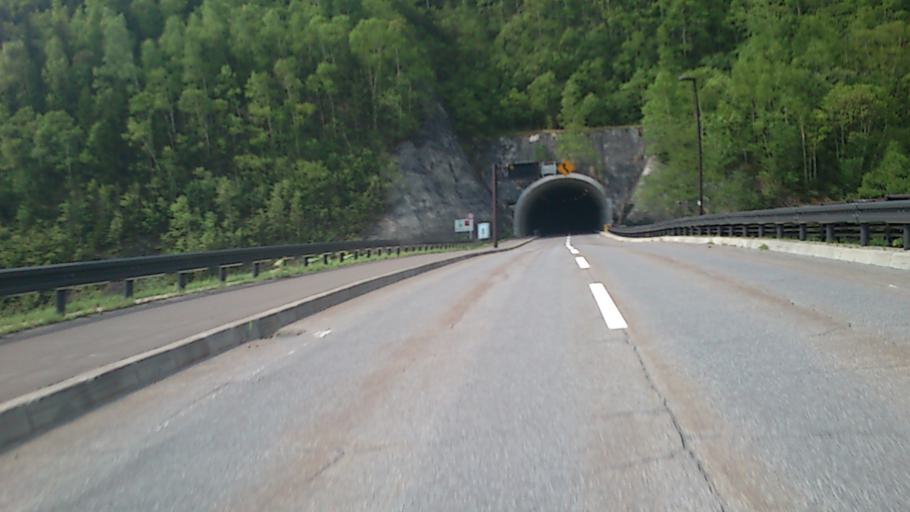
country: JP
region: Hokkaido
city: Kamikawa
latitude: 43.6756
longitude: 143.0361
